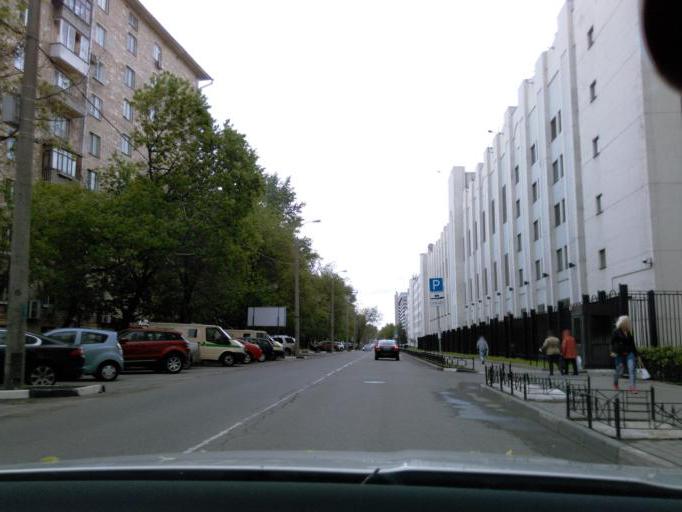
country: RU
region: Moskovskaya
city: Dorogomilovo
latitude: 55.7845
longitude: 37.5776
